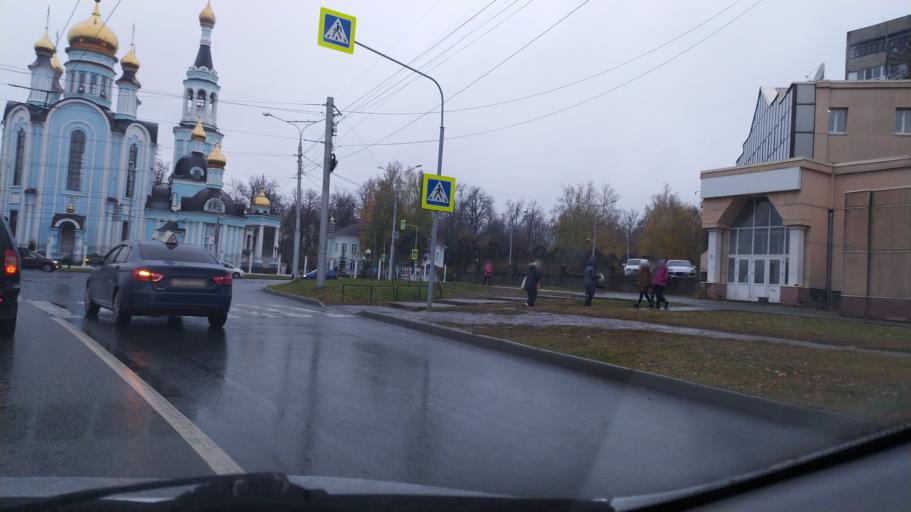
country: RU
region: Chuvashia
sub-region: Cheboksarskiy Rayon
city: Cheboksary
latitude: 56.1415
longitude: 47.1860
